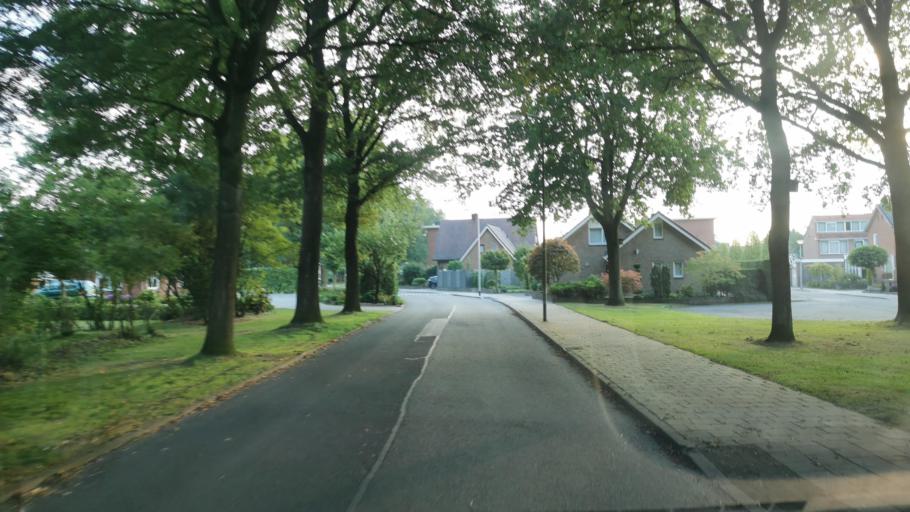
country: NL
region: Overijssel
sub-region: Gemeente Oldenzaal
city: Oldenzaal
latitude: 52.3029
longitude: 6.9441
